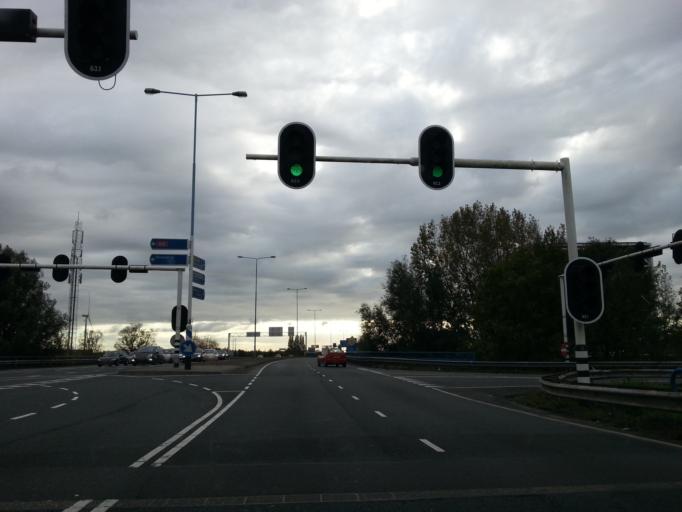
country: NL
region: South Holland
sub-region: Gemeente Zoetermeer
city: Zoetermeer
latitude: 52.0444
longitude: 4.5086
